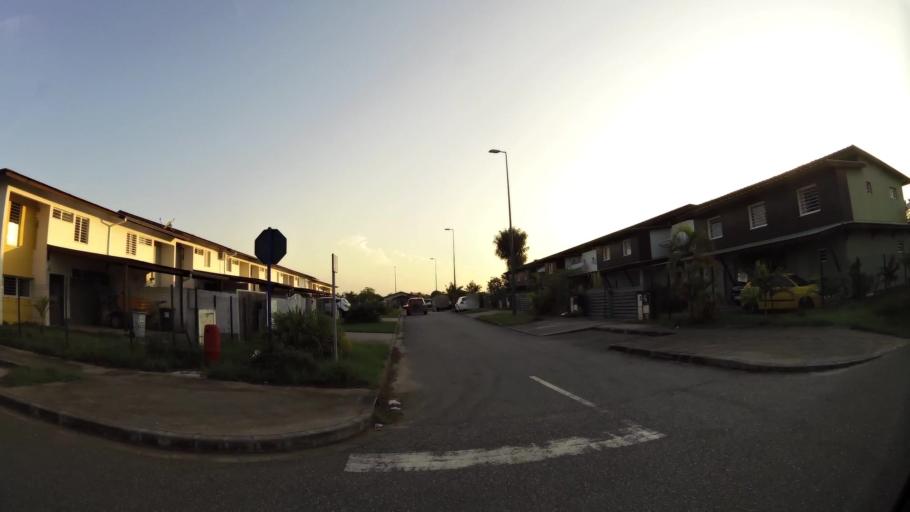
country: GF
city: Macouria
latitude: 4.9320
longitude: -52.4109
